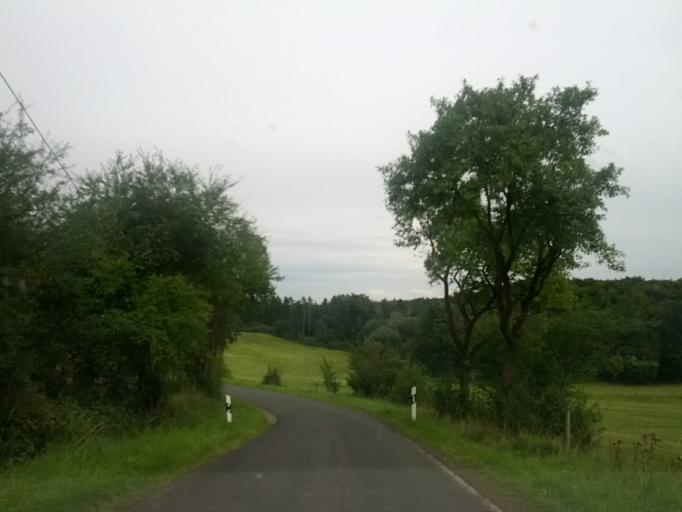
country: DE
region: Thuringia
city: Wolfsburg-Unkeroda
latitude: 50.9049
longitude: 10.2584
